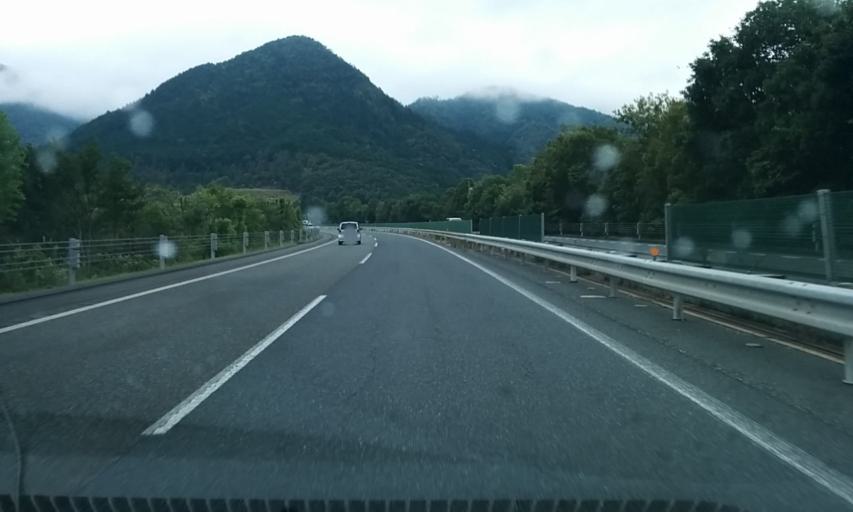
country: JP
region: Hyogo
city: Sasayama
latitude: 35.1436
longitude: 135.1273
